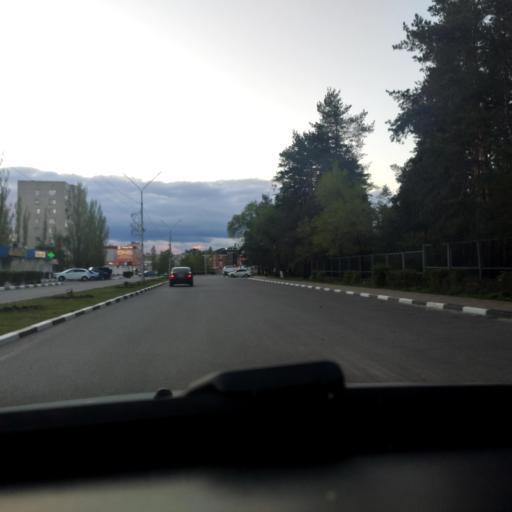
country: RU
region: Voronezj
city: Novovoronezh
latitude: 51.3130
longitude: 39.2086
